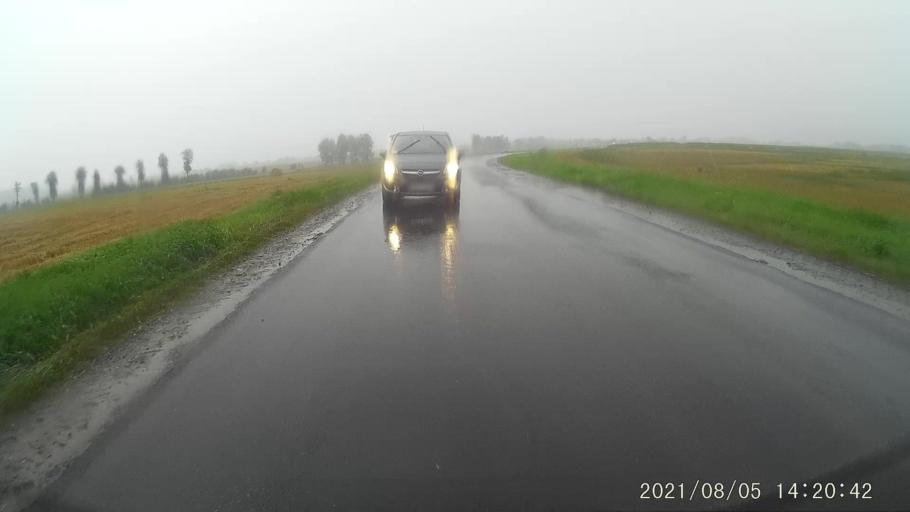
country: PL
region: Opole Voivodeship
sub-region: Powiat nyski
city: Korfantow
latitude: 50.4704
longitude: 17.6789
